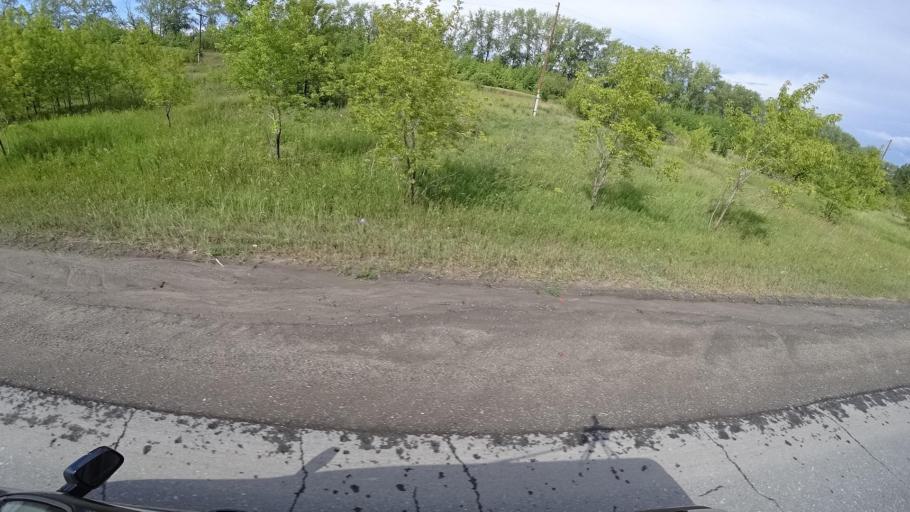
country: RU
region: Sverdlovsk
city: Kamyshlov
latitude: 56.8435
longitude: 62.7742
